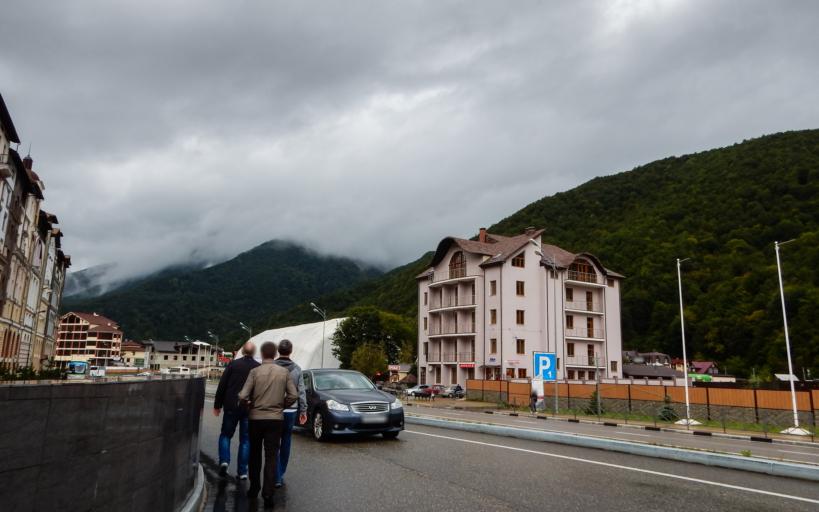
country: RU
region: Krasnodarskiy
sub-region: Sochi City
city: Krasnaya Polyana
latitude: 43.6837
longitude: 40.2665
